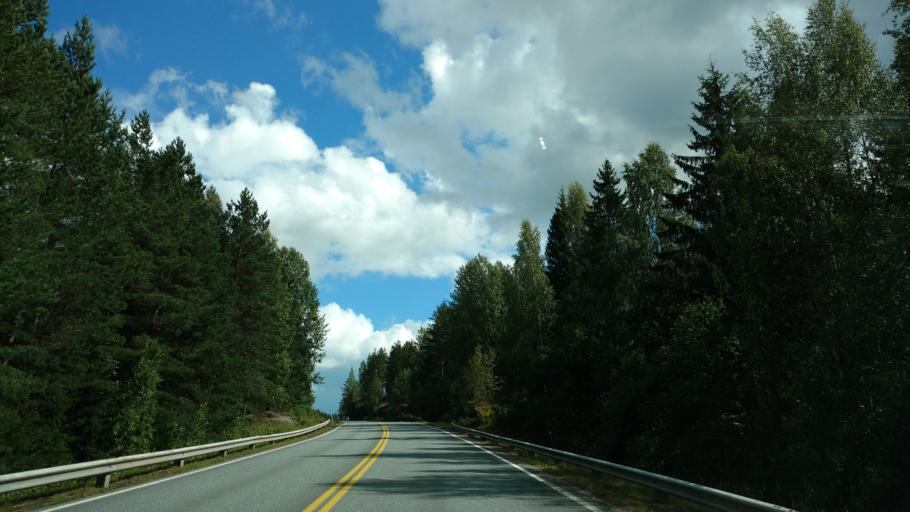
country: FI
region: Uusimaa
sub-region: Helsinki
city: Karjalohja
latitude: 60.2165
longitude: 23.6310
